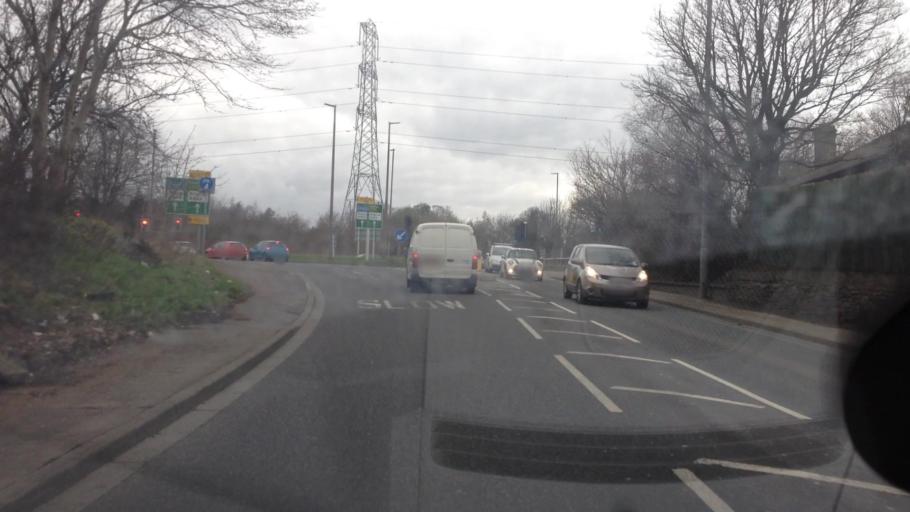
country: GB
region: England
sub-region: Calderdale
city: Elland
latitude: 53.6683
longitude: -1.8248
